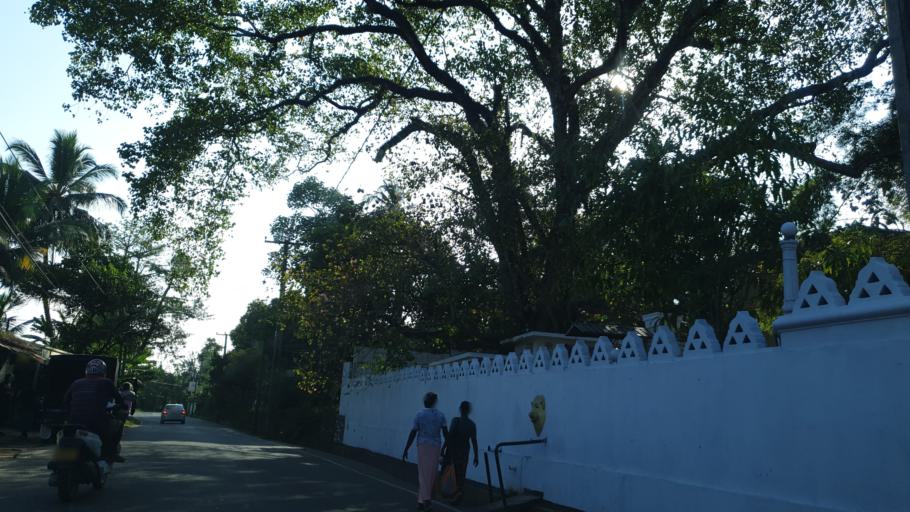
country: LK
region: Western
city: Sri Jayewardenepura Kotte
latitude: 6.8752
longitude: 79.9187
